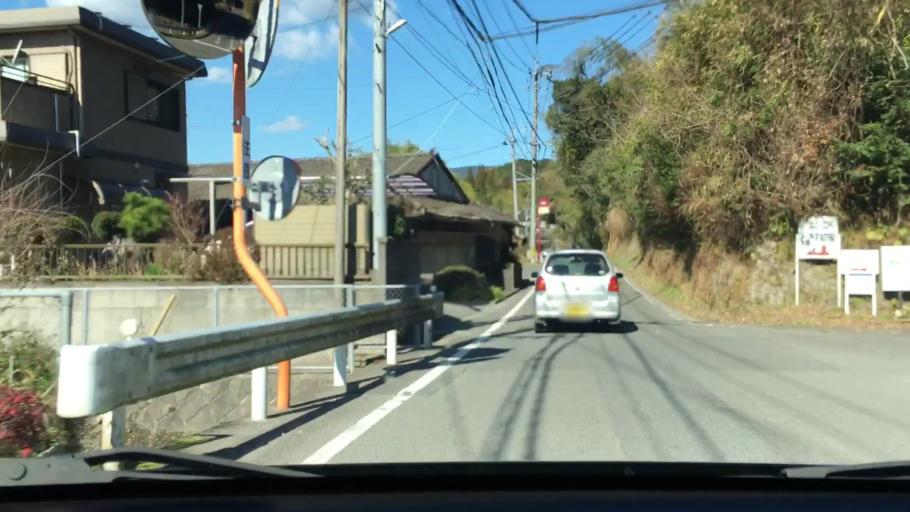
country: JP
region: Kagoshima
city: Ijuin
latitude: 31.6858
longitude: 130.4683
